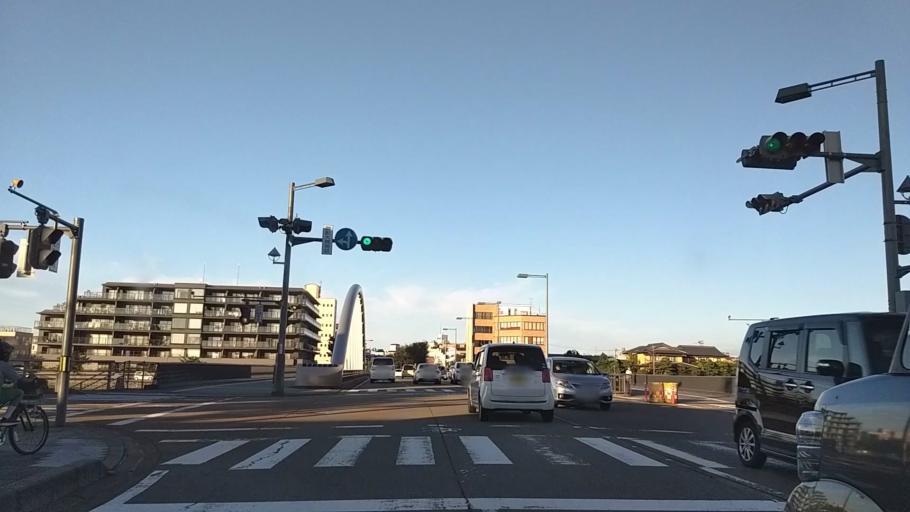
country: JP
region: Ishikawa
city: Kanazawa-shi
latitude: 36.5633
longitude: 136.6429
